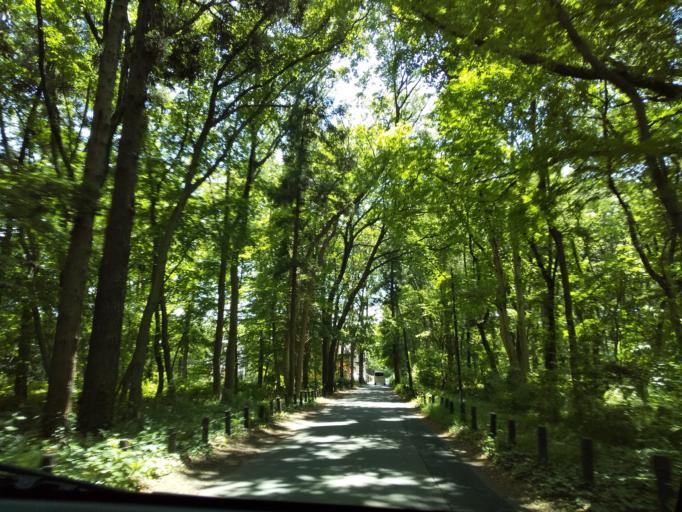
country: JP
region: Tokyo
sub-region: Machida-shi
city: Machida
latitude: 35.5428
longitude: 139.4081
